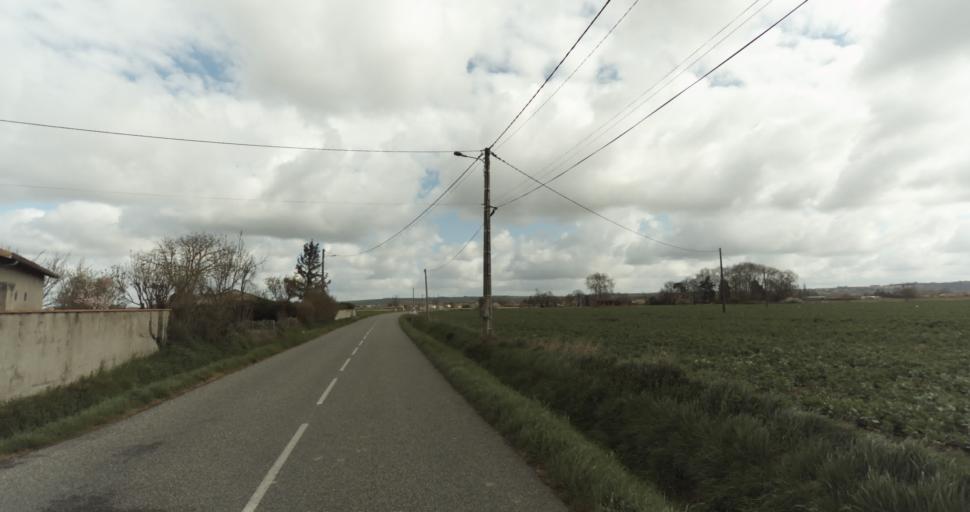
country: FR
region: Midi-Pyrenees
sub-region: Departement de la Haute-Garonne
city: Auterive
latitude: 43.3373
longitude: 1.4578
